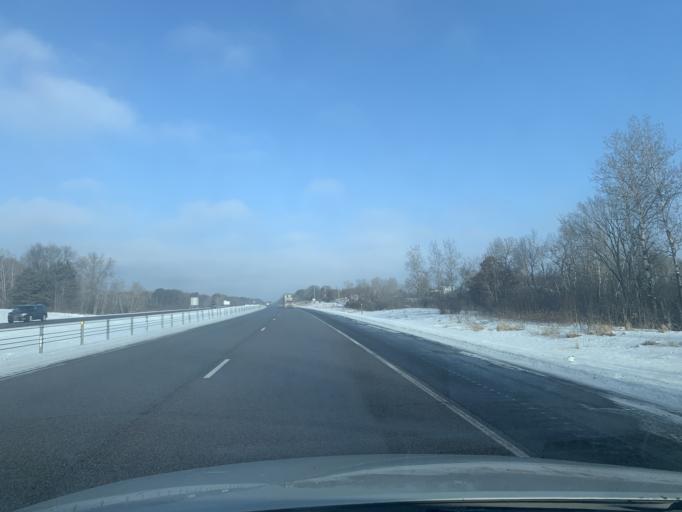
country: US
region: Minnesota
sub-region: Washington County
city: Forest Lake
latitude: 45.3016
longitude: -93.0025
